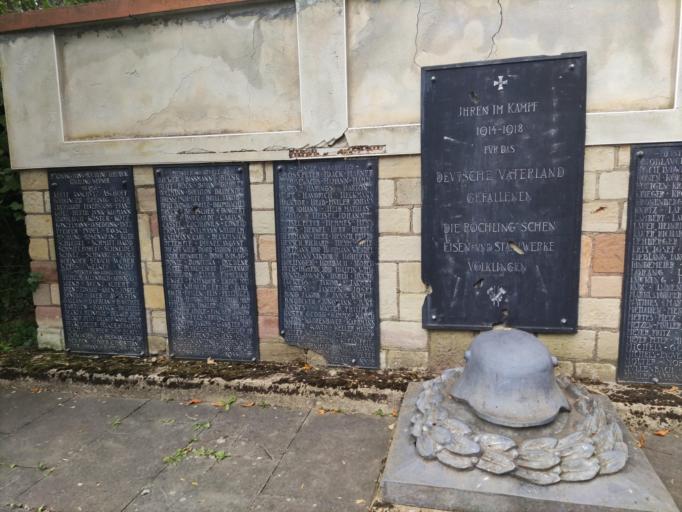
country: DE
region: Saarland
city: Volklingen
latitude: 49.2615
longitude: 6.8573
